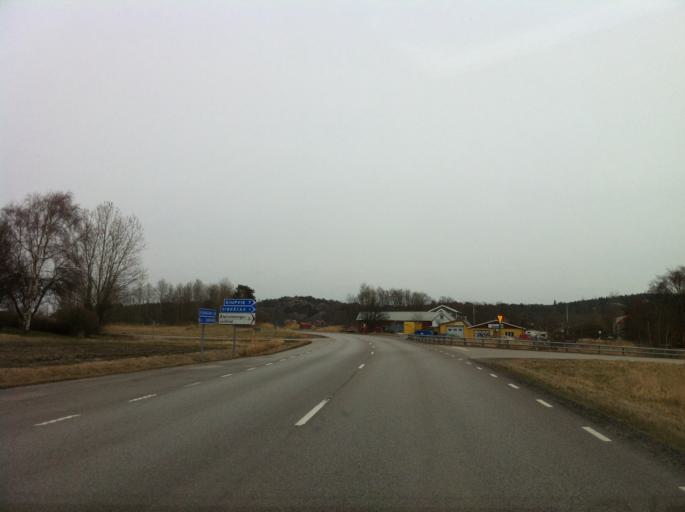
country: SE
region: Vaestra Goetaland
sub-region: Tjorns Kommun
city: Skaerhamn
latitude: 58.0013
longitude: 11.6048
